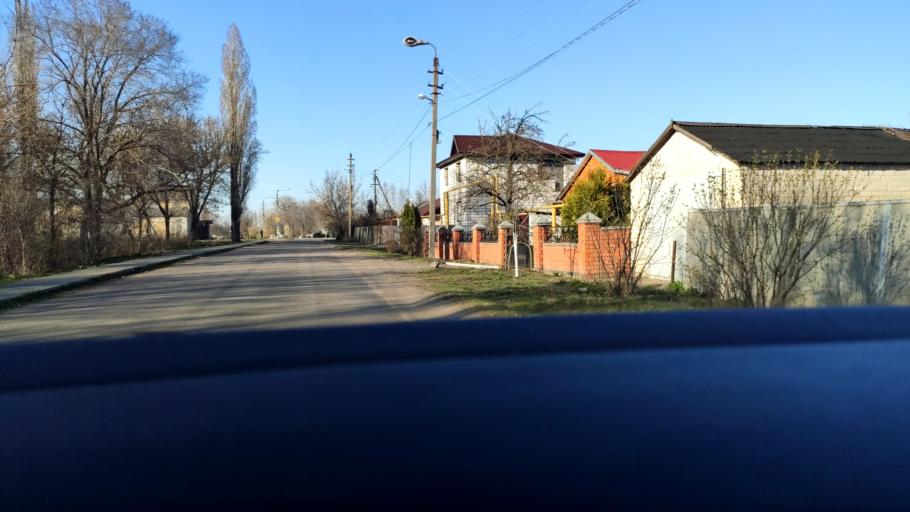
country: RU
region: Voronezj
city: Maslovka
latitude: 51.5047
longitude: 39.2936
